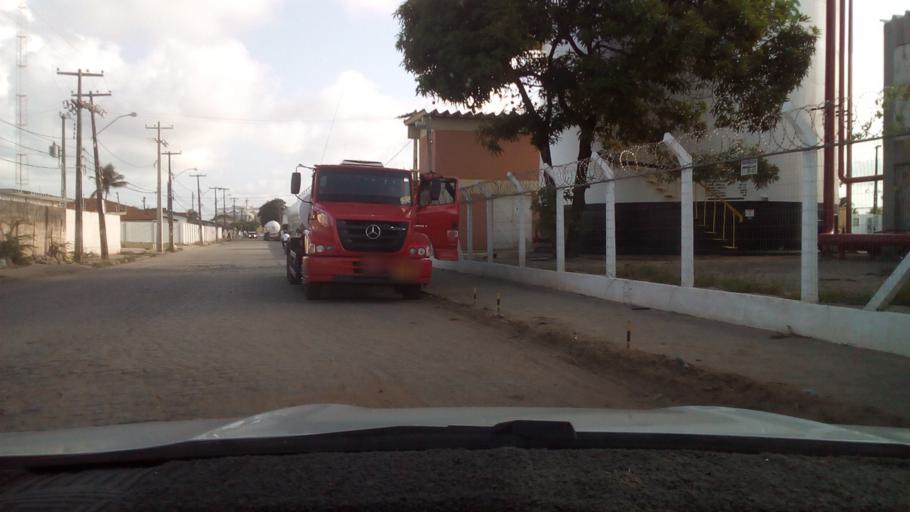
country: BR
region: Paraiba
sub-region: Cabedelo
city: Cabedelo
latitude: -6.9665
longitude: -34.8380
